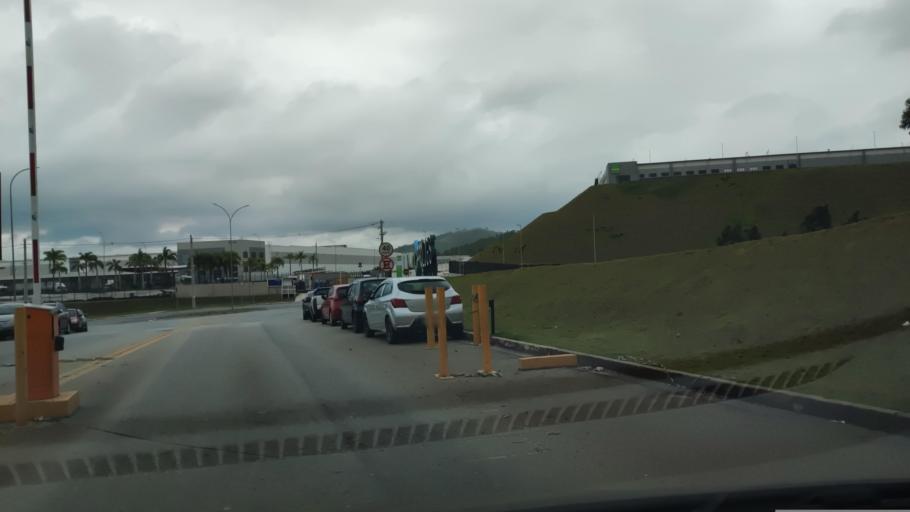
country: BR
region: Sao Paulo
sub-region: Cajamar
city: Cajamar
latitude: -23.3328
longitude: -46.8504
